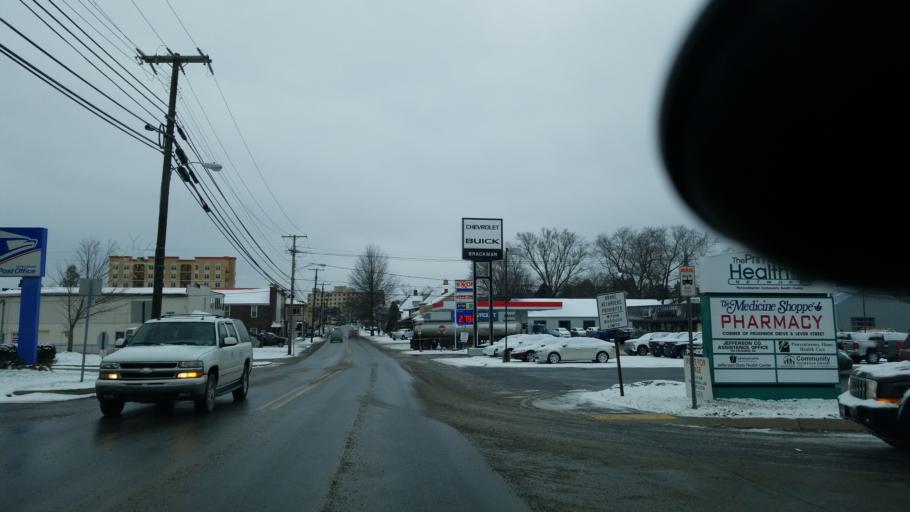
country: US
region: Pennsylvania
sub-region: Jefferson County
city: Punxsutawney
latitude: 40.9444
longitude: -78.9625
